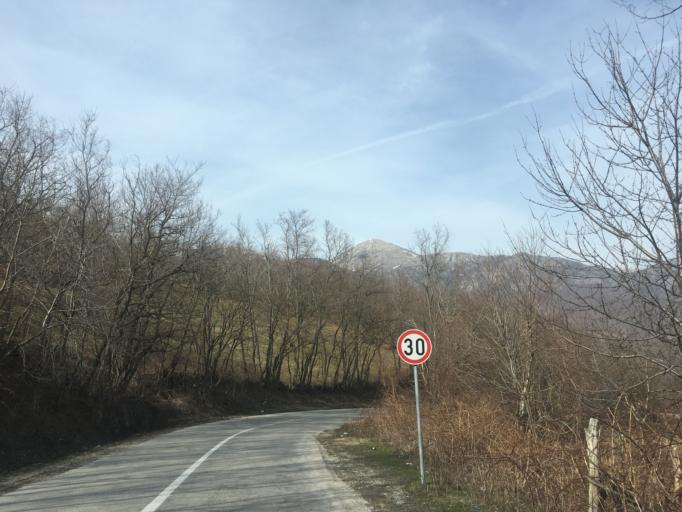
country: XK
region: Pec
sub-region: Komuna e Pejes
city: Dubova (Driloni)
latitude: 42.7504
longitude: 20.3079
